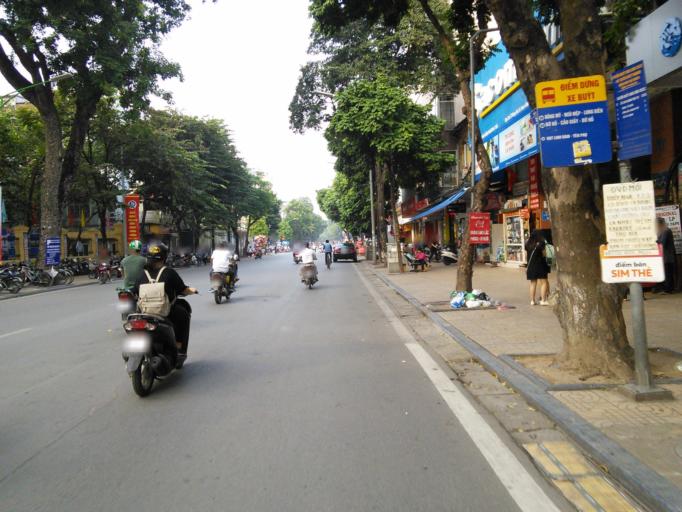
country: VN
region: Ha Noi
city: Hoan Kiem
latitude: 21.0231
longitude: 105.8528
